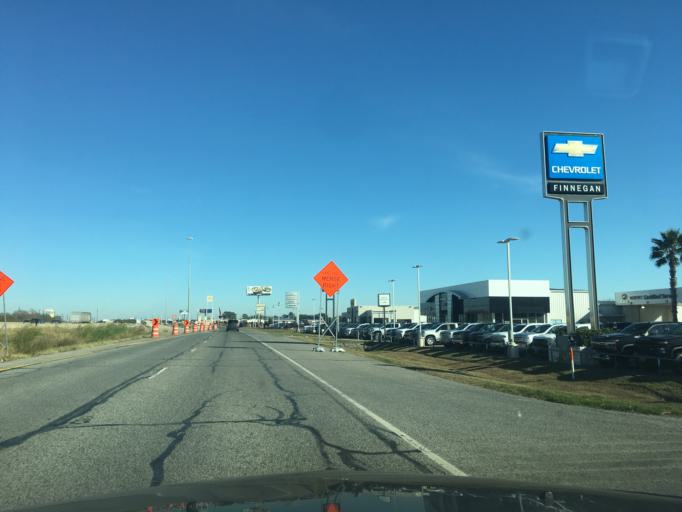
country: US
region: Texas
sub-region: Fort Bend County
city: Rosenberg
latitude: 29.5325
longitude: -95.7853
